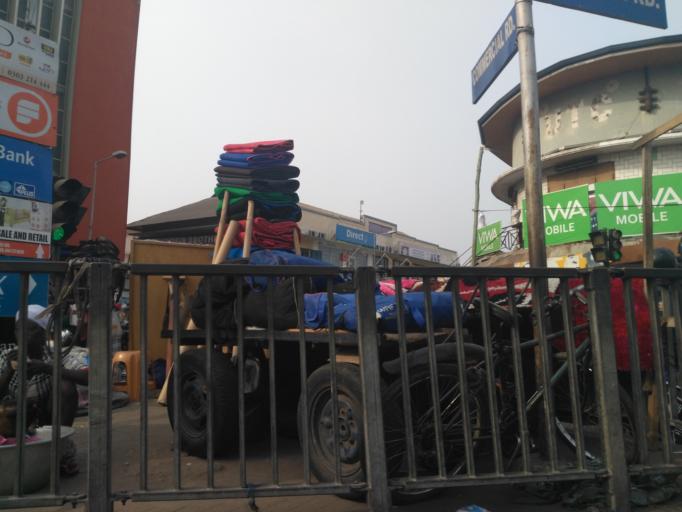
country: GH
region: Greater Accra
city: Accra
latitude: 5.5469
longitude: -0.2104
